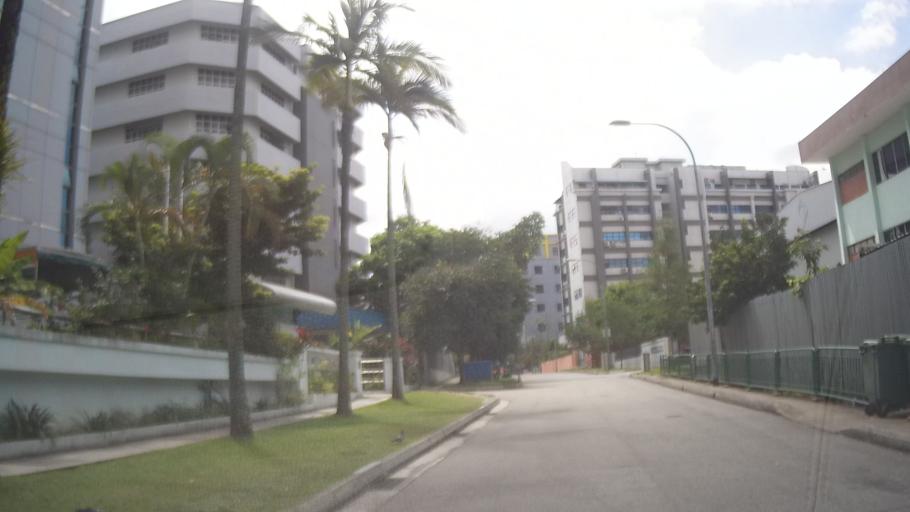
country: MY
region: Johor
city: Johor Bahru
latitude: 1.4082
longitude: 103.7597
